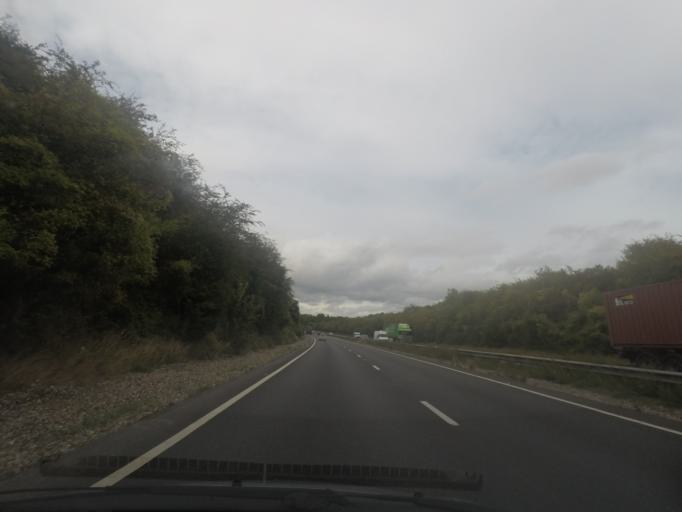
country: GB
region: England
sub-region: Hampshire
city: Overton
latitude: 51.2441
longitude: -1.3411
